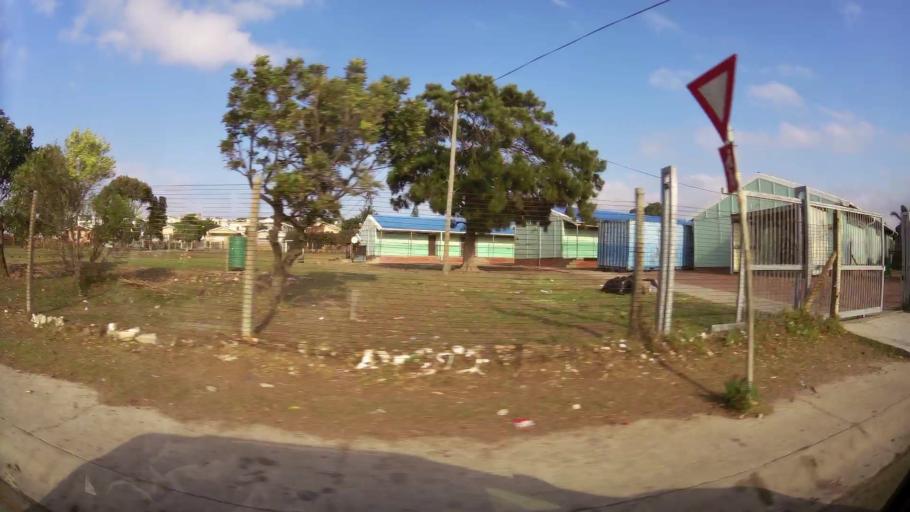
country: ZA
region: Eastern Cape
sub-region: Nelson Mandela Bay Metropolitan Municipality
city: Port Elizabeth
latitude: -33.9256
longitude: 25.5568
